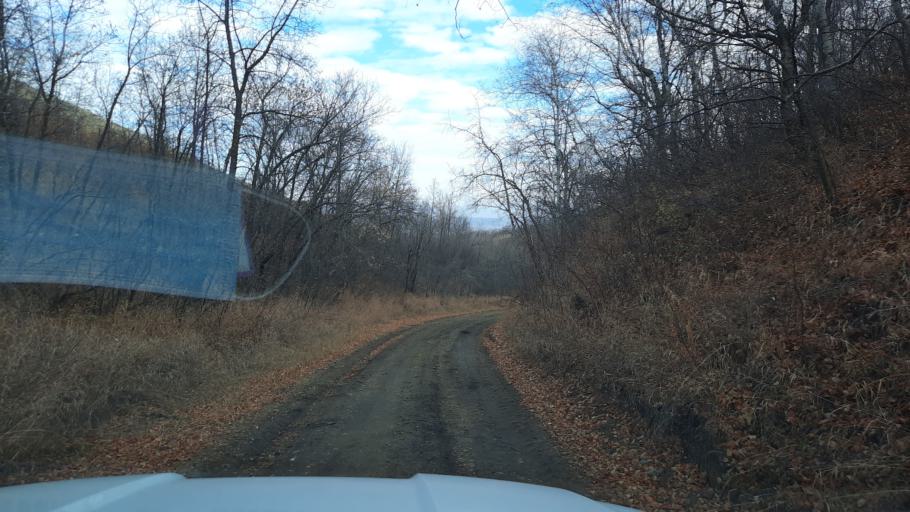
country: CA
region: Saskatchewan
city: Pilot Butte
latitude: 50.7756
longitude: -104.2139
